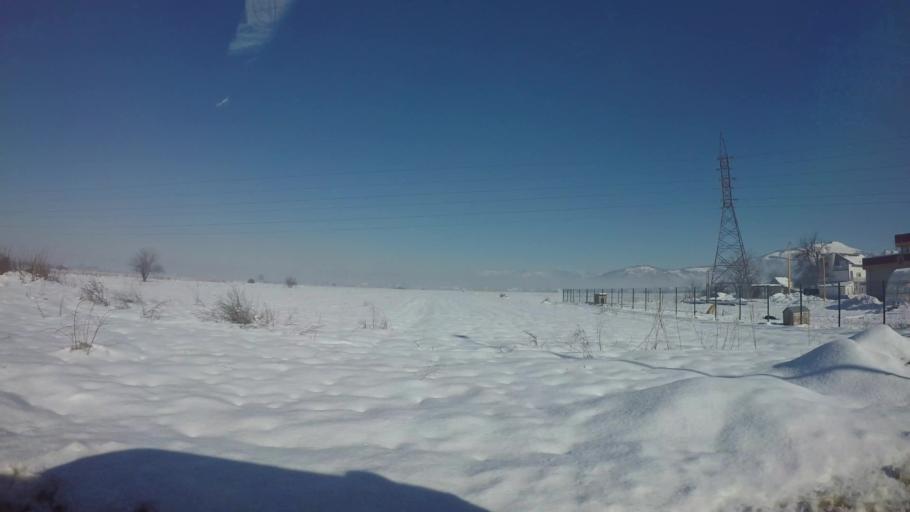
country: BA
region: Federation of Bosnia and Herzegovina
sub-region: Kanton Sarajevo
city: Sarajevo
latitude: 43.7921
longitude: 18.3327
